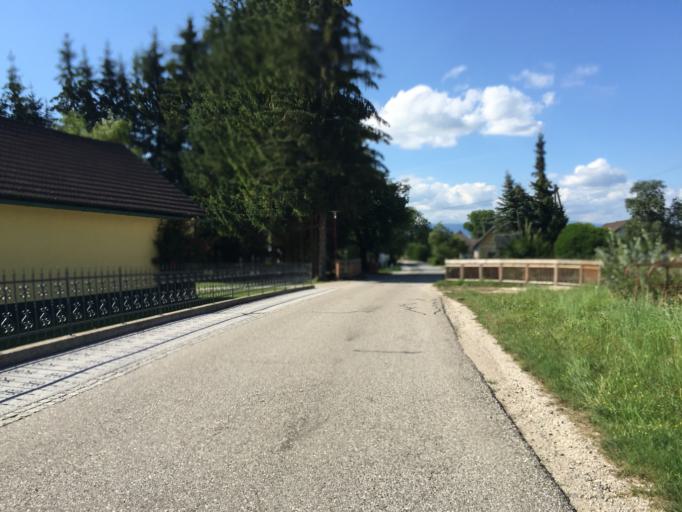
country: AT
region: Carinthia
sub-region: Politischer Bezirk Volkermarkt
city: Feistritz ob Bleiburg
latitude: 46.5636
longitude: 14.7569
